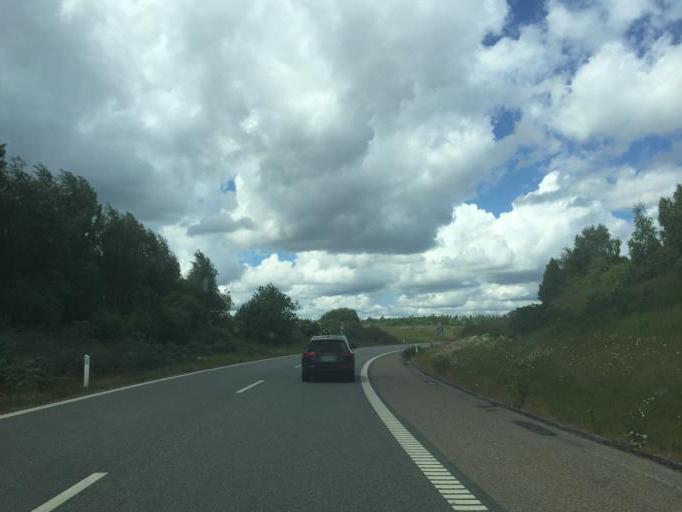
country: DK
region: Capital Region
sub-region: Kobenhavn
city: Copenhagen
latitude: 55.6301
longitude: 12.5470
